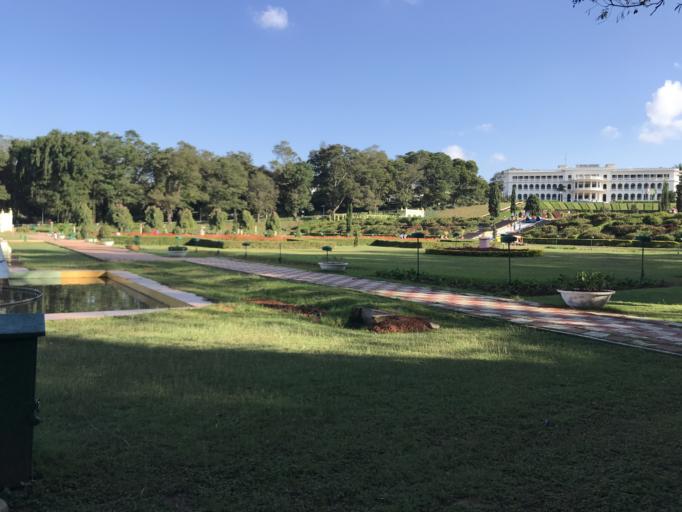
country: IN
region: Karnataka
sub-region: Mandya
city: Shrirangapattana
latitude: 12.4217
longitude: 76.5722
